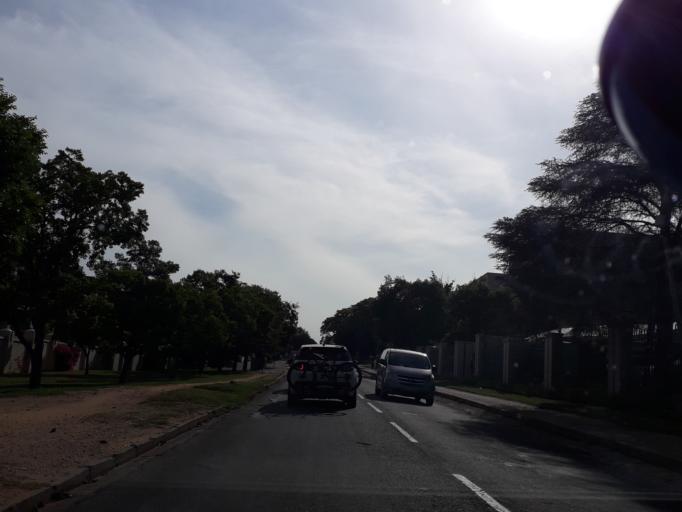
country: ZA
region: Gauteng
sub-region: City of Johannesburg Metropolitan Municipality
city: Johannesburg
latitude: -26.0746
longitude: 28.0326
